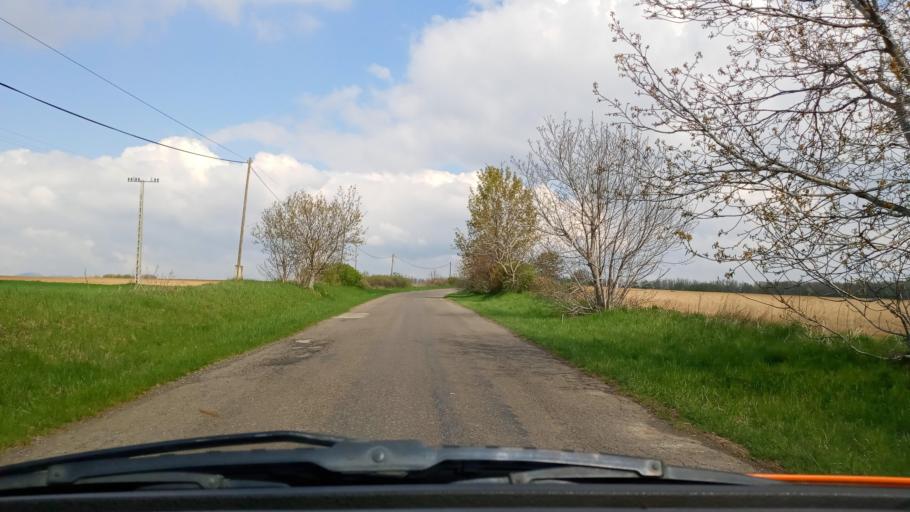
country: HU
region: Baranya
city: Pecsvarad
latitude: 46.1020
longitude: 18.4968
